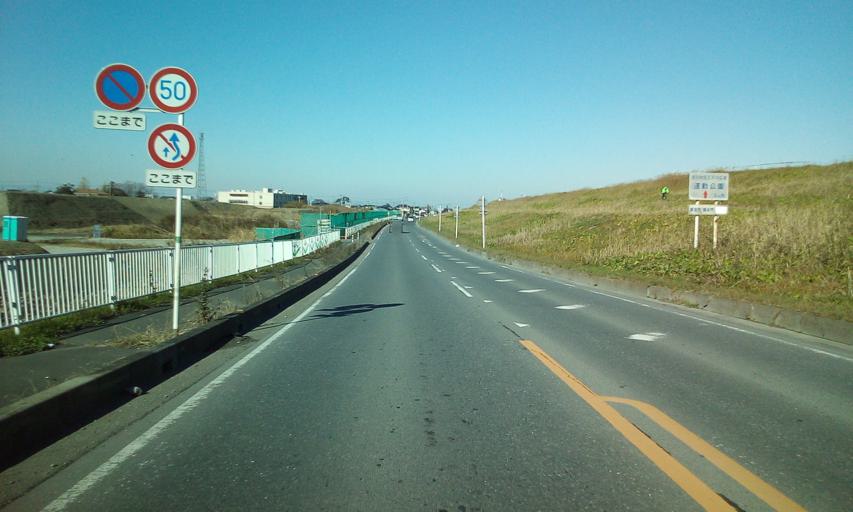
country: JP
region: Chiba
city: Noda
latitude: 35.9125
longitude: 139.8698
